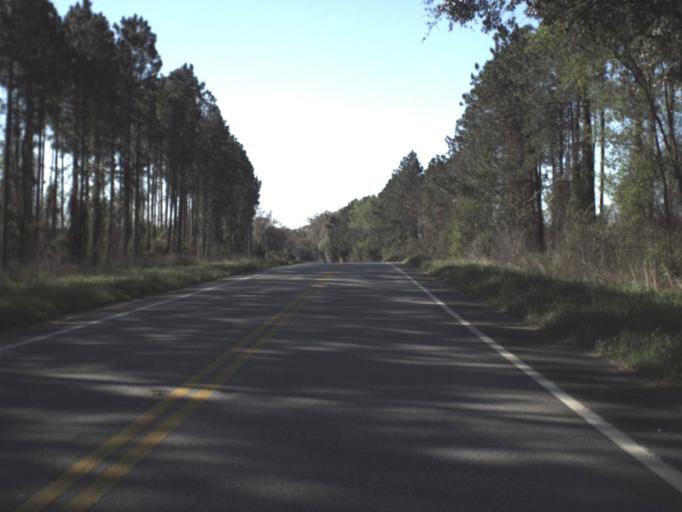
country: US
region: Georgia
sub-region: Brooks County
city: Quitman
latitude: 30.6108
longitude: -83.6465
